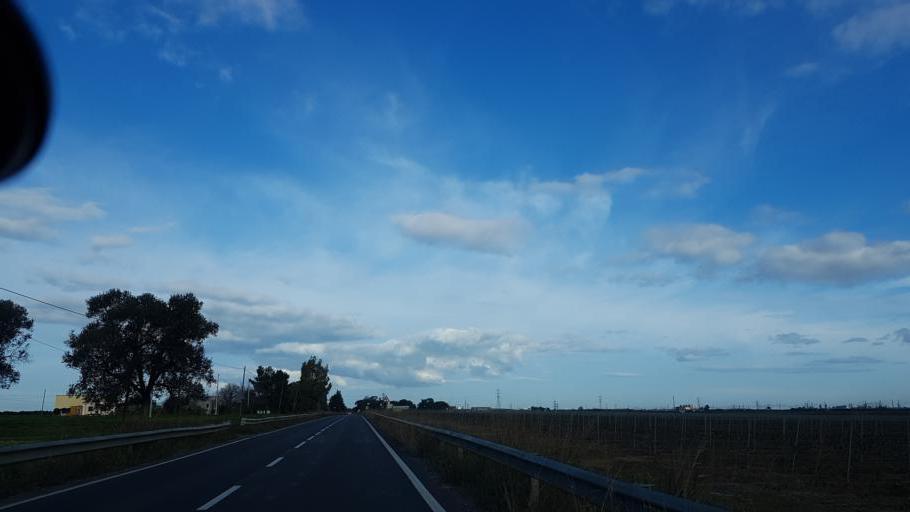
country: IT
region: Apulia
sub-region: Provincia di Brindisi
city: La Rosa
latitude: 40.5776
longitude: 17.9657
